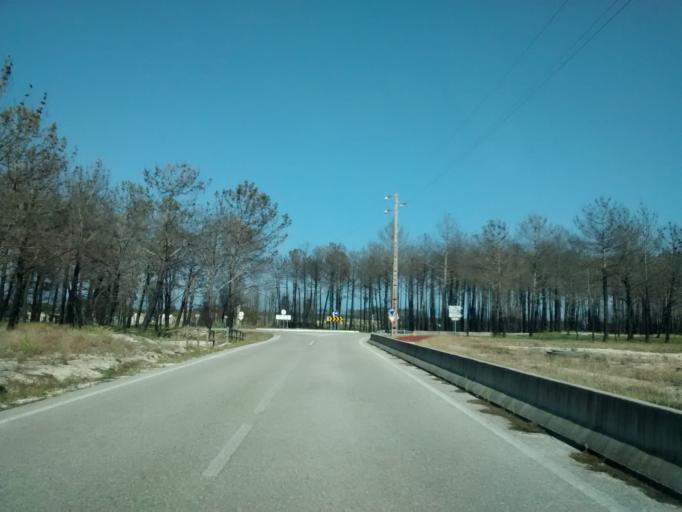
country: PT
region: Coimbra
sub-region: Figueira da Foz
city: Lavos
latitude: 40.0003
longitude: -8.8644
